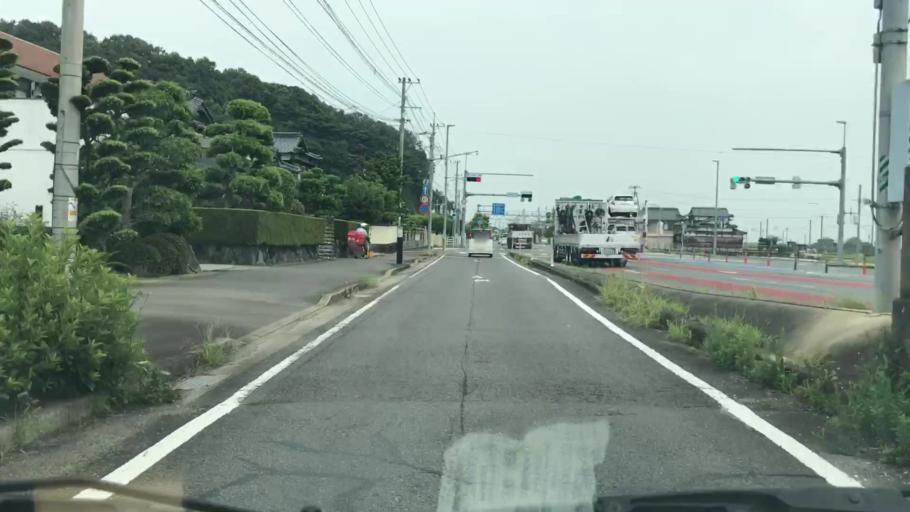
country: JP
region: Saga Prefecture
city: Saga-shi
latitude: 33.2242
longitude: 130.1750
